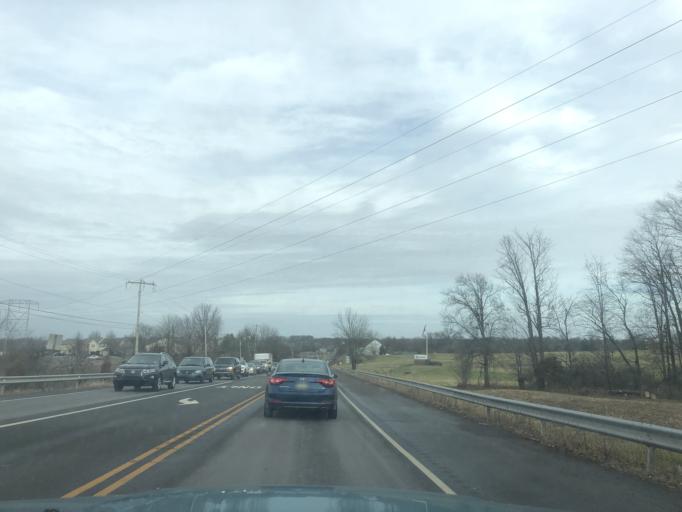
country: US
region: Pennsylvania
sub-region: Montgomery County
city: Harleysville
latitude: 40.2783
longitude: -75.3963
